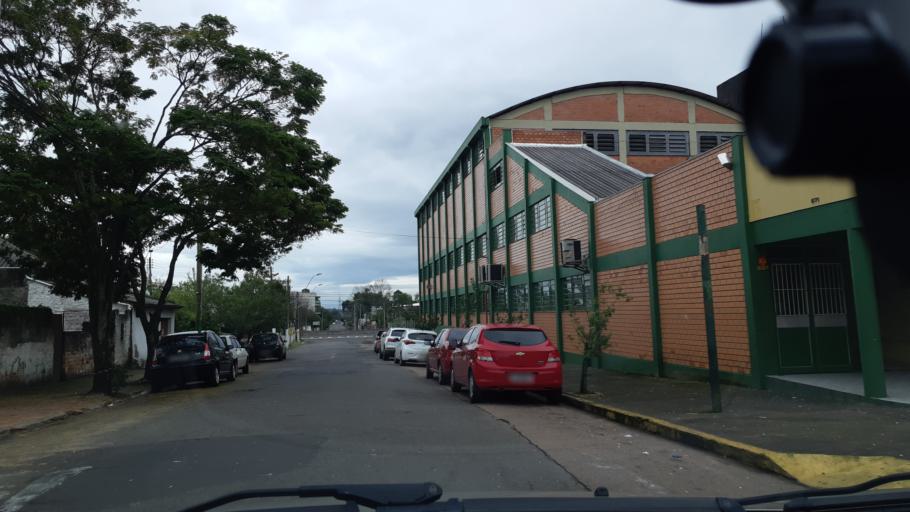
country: BR
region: Rio Grande do Sul
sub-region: Sao Leopoldo
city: Sao Leopoldo
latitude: -29.7757
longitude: -51.1535
